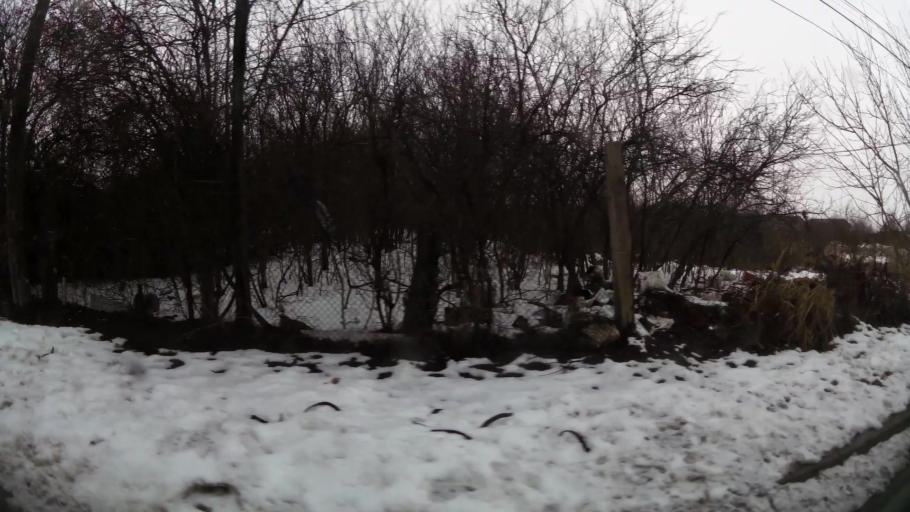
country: RO
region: Ilfov
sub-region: Comuna Mogosoaia
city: Mogosoaia
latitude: 44.5154
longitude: 26.0237
